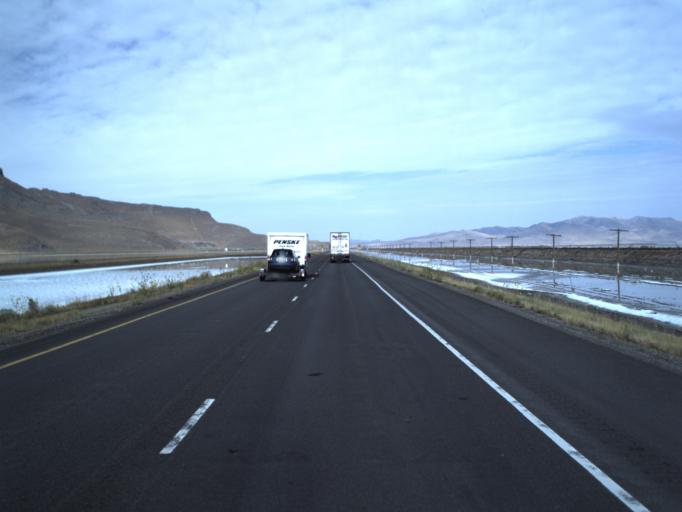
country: US
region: Utah
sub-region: Tooele County
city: Grantsville
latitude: 40.7291
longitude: -112.5838
